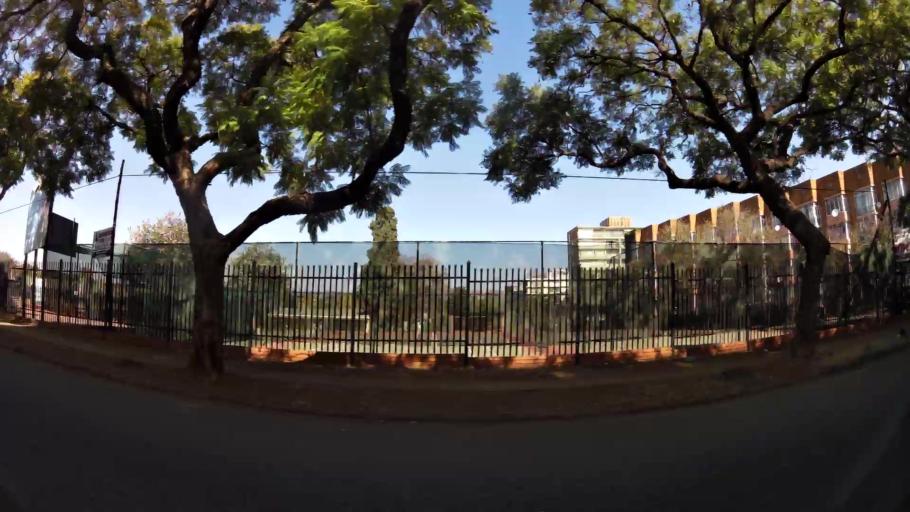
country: ZA
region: Gauteng
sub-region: City of Tshwane Metropolitan Municipality
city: Pretoria
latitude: -25.7459
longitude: 28.2181
